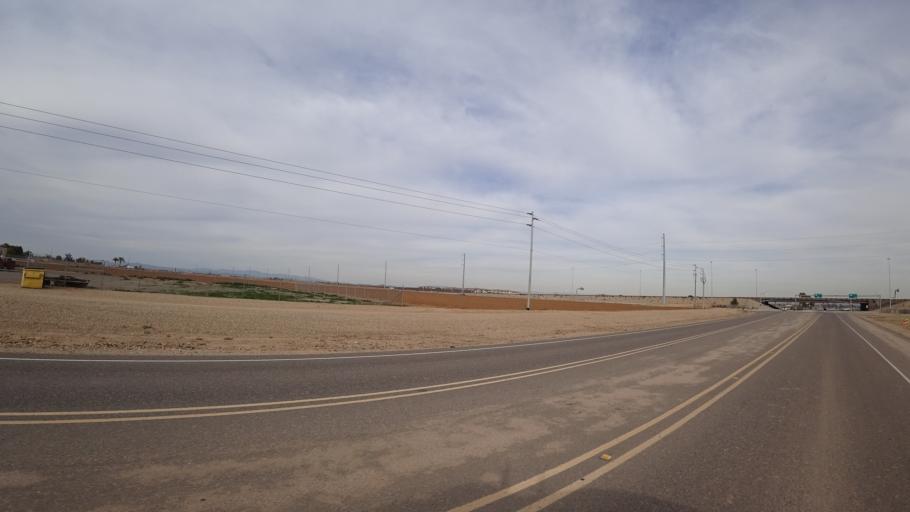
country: US
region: Arizona
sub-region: Maricopa County
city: Citrus Park
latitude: 33.5807
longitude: -112.4220
